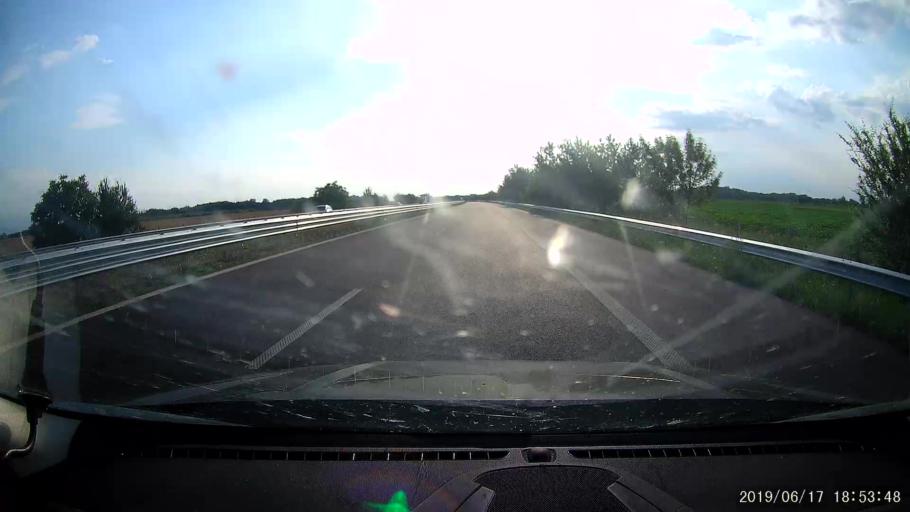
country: BG
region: Plovdiv
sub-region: Obshtina Sadovo
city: Sadovo
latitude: 42.2173
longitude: 24.9008
